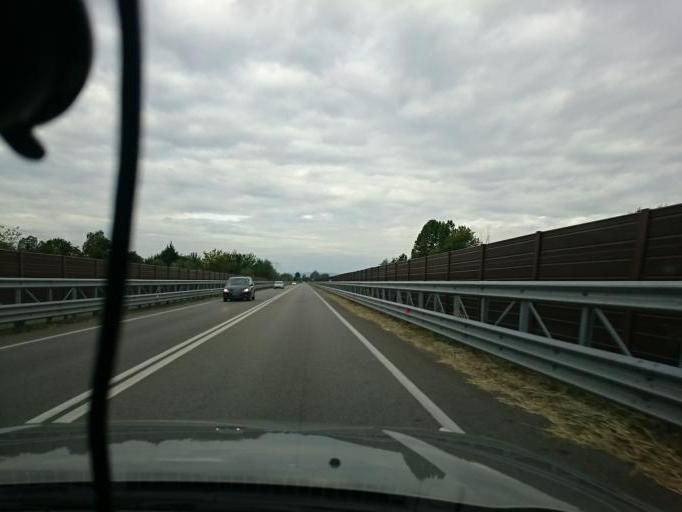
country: IT
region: Veneto
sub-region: Provincia di Padova
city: Selvazzano Dentro
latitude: 45.3802
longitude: 11.7904
